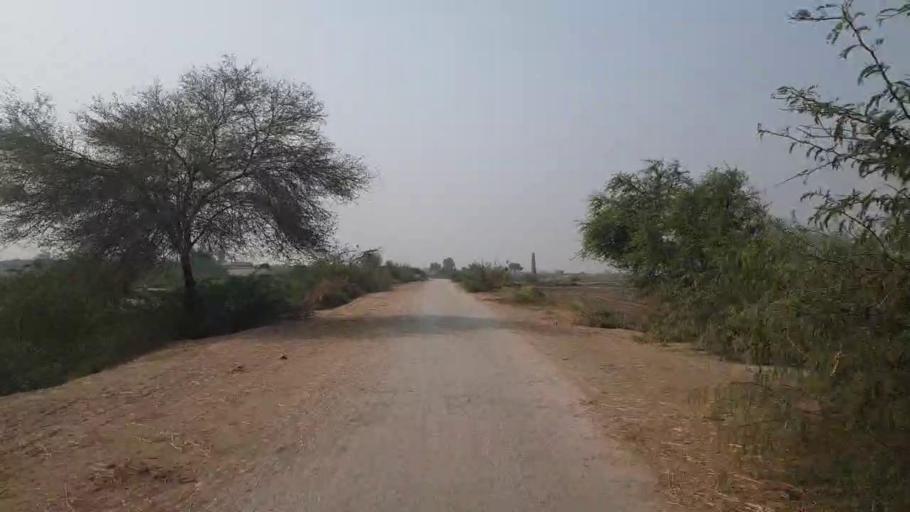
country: PK
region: Sindh
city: Tando Jam
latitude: 25.2903
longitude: 68.4987
